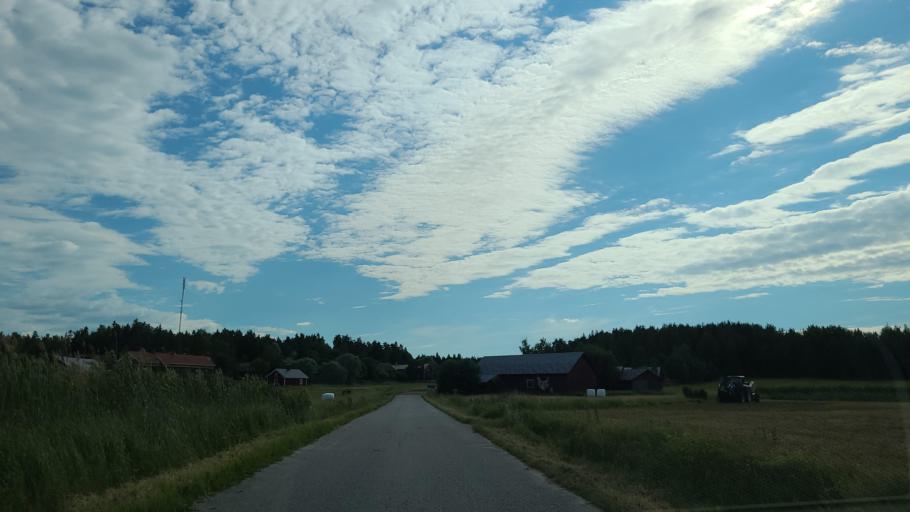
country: FI
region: Varsinais-Suomi
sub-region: Turku
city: Rymaettylae
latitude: 60.2906
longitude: 21.9333
